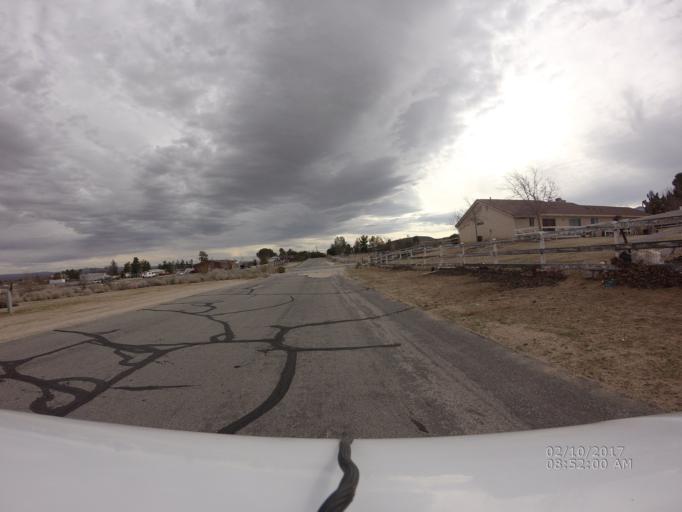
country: US
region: California
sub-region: Los Angeles County
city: Littlerock
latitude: 34.4845
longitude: -117.8995
